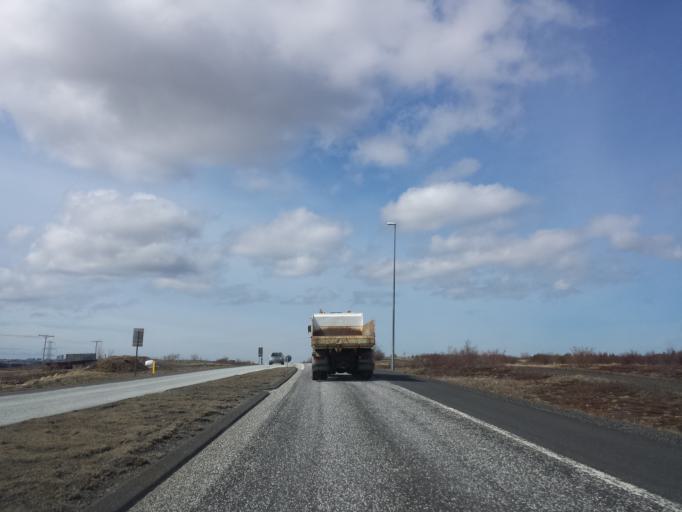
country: IS
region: Capital Region
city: Mosfellsbaer
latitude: 64.0930
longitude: -21.7157
